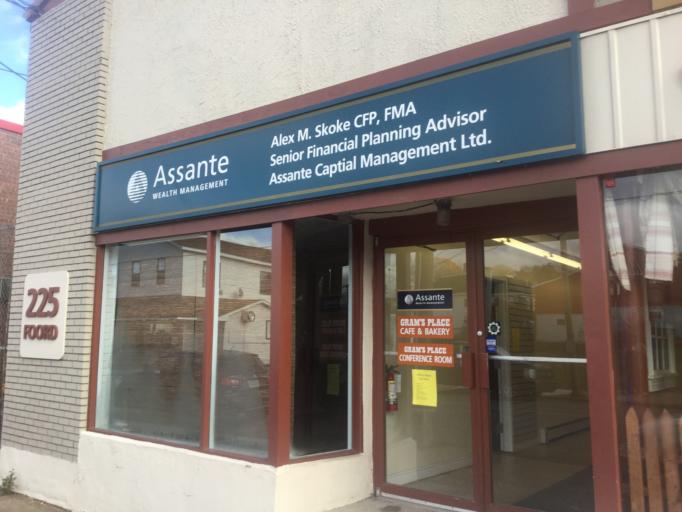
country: CA
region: Nova Scotia
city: New Glasgow
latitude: 45.5602
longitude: -62.6596
